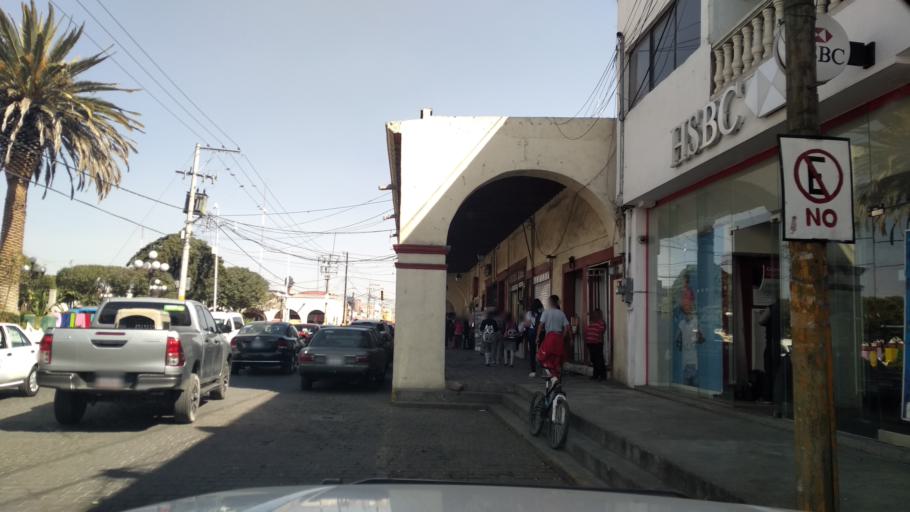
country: MX
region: Hidalgo
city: Calpulalpan
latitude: 19.5881
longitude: -98.5712
